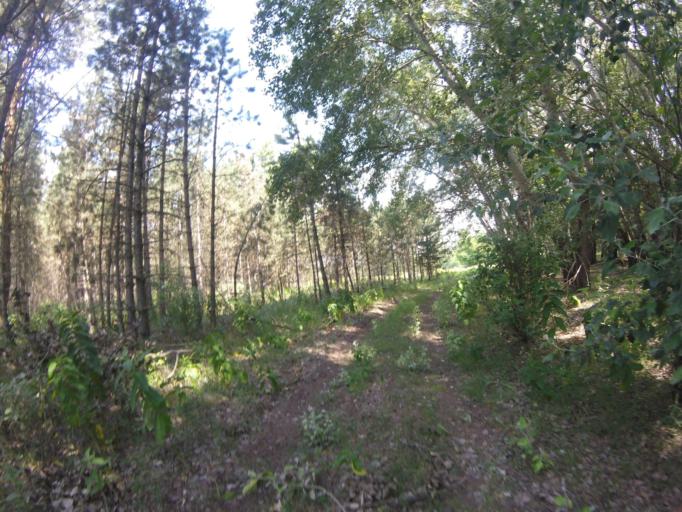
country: HU
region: Bacs-Kiskun
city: Jaszszentlaszlo
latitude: 46.6075
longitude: 19.7186
